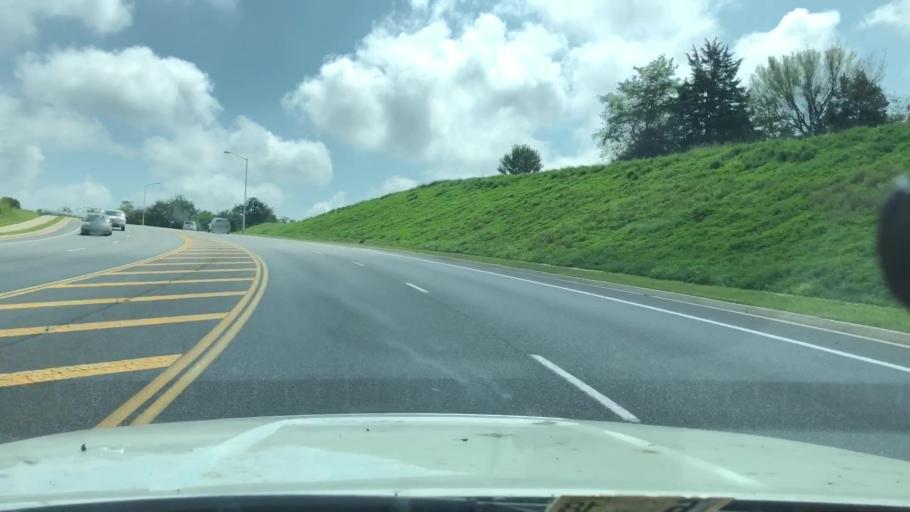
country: US
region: Virginia
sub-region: City of Harrisonburg
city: Harrisonburg
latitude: 38.4300
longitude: -78.9024
